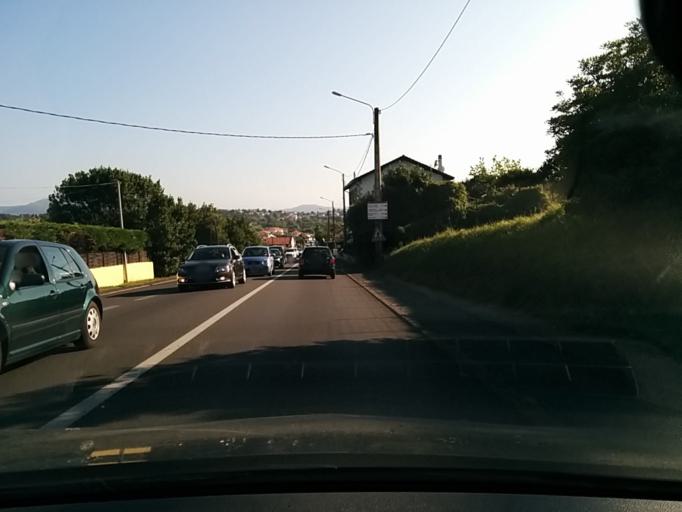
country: FR
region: Aquitaine
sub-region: Departement des Pyrenees-Atlantiques
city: Bidart
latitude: 43.4370
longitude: -1.5923
